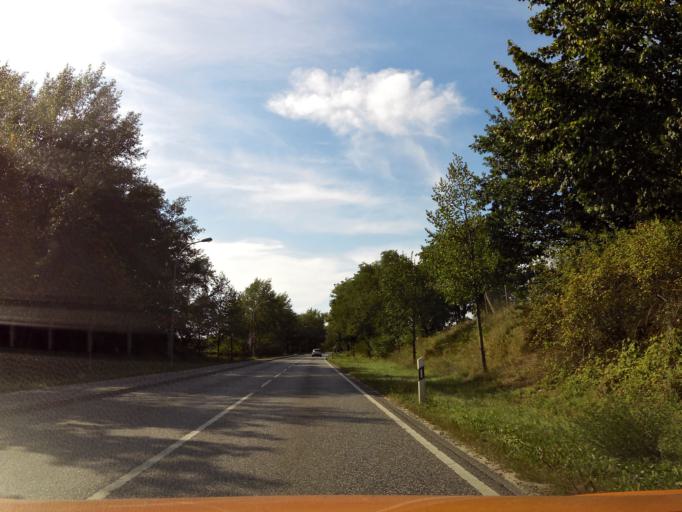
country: DE
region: Brandenburg
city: Teltow
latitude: 52.3780
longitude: 13.2576
